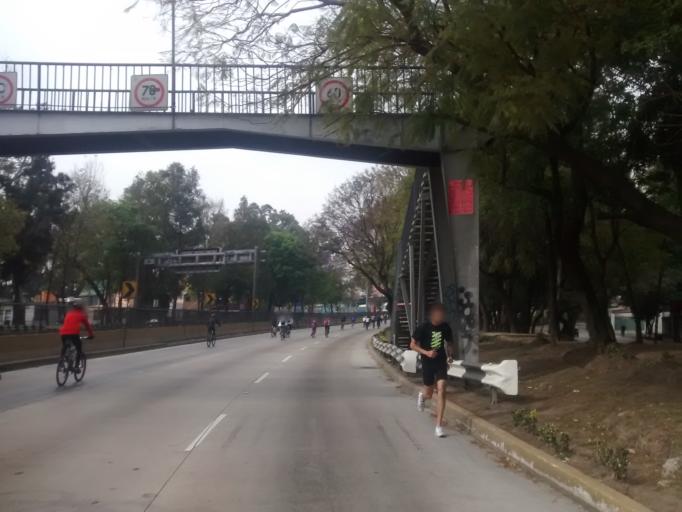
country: MX
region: Mexico City
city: Colonia Nativitas
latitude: 19.3573
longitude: -99.1323
